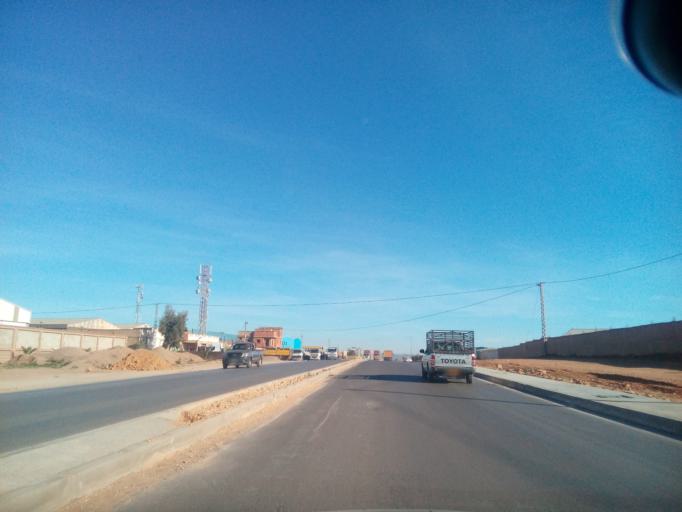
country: DZ
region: Mostaganem
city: Mostaganem
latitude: 35.9118
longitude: 0.1466
